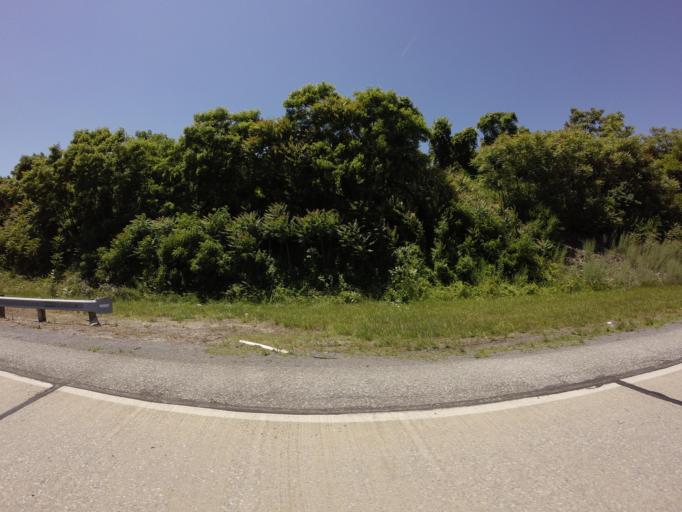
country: US
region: West Virginia
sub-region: Jefferson County
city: Ranson
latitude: 39.3007
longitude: -77.8407
